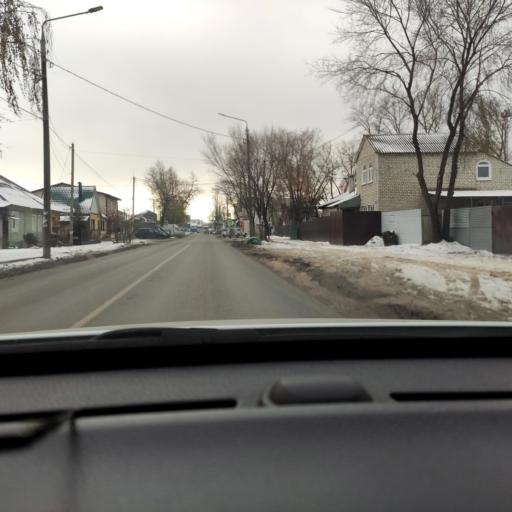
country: RU
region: Voronezj
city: Somovo
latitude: 51.7365
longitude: 39.2670
